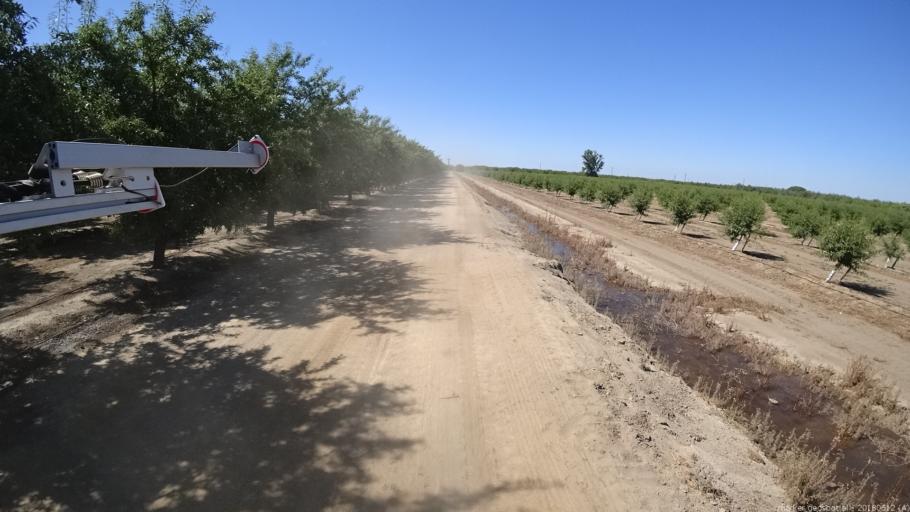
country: US
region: California
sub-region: Fresno County
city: Firebaugh
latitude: 37.0315
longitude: -120.4148
